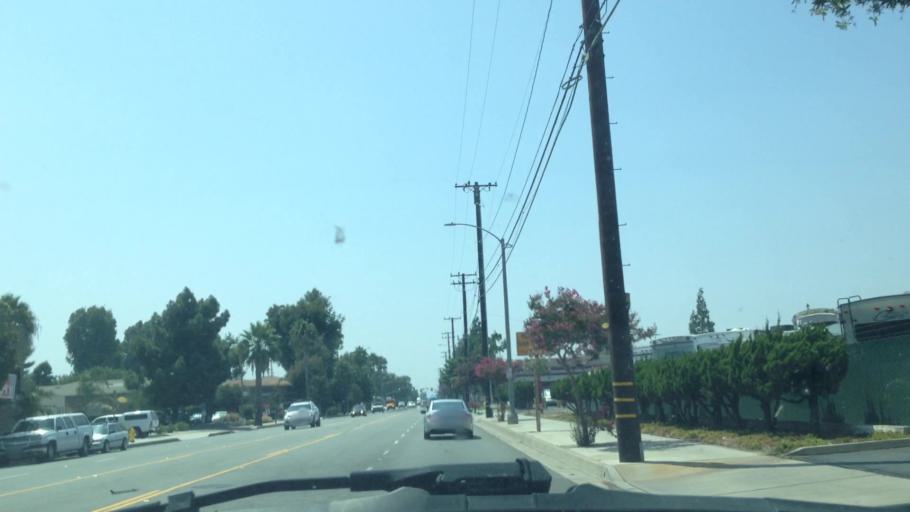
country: US
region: California
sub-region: Orange County
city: Buena Park
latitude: 33.8702
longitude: -117.9640
